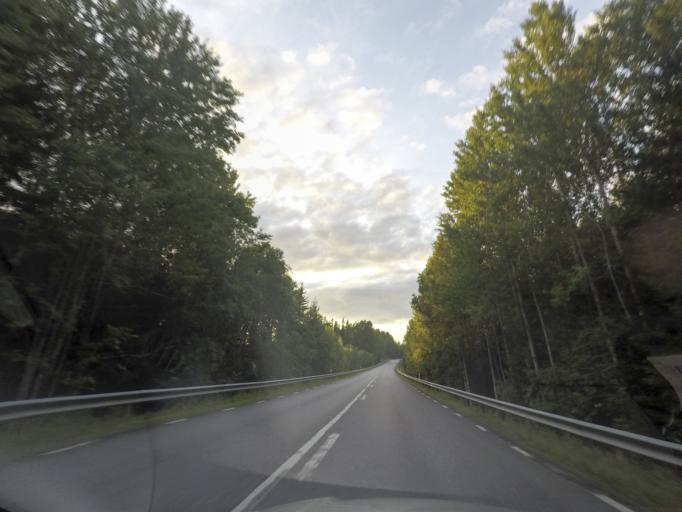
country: SE
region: OErebro
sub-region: Hallefors Kommun
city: Haellefors
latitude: 59.7129
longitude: 14.5333
